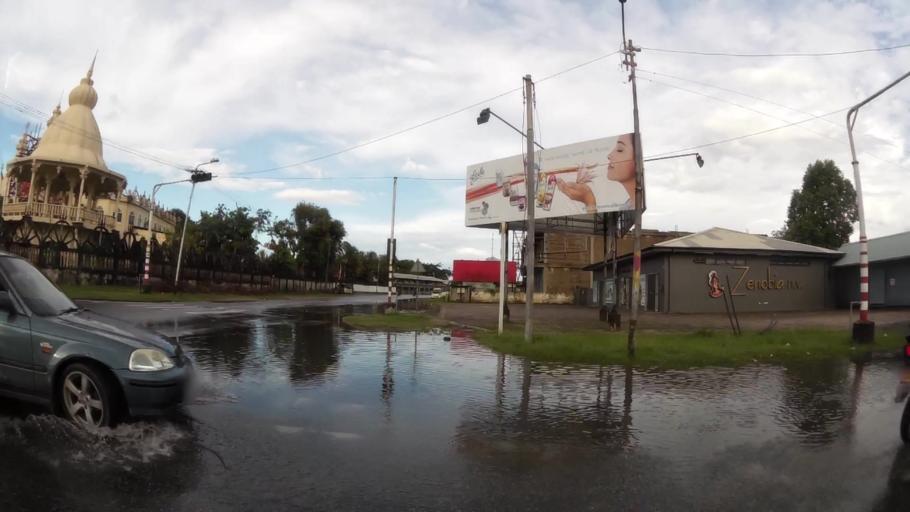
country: SR
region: Paramaribo
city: Paramaribo
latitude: 5.8267
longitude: -55.1812
